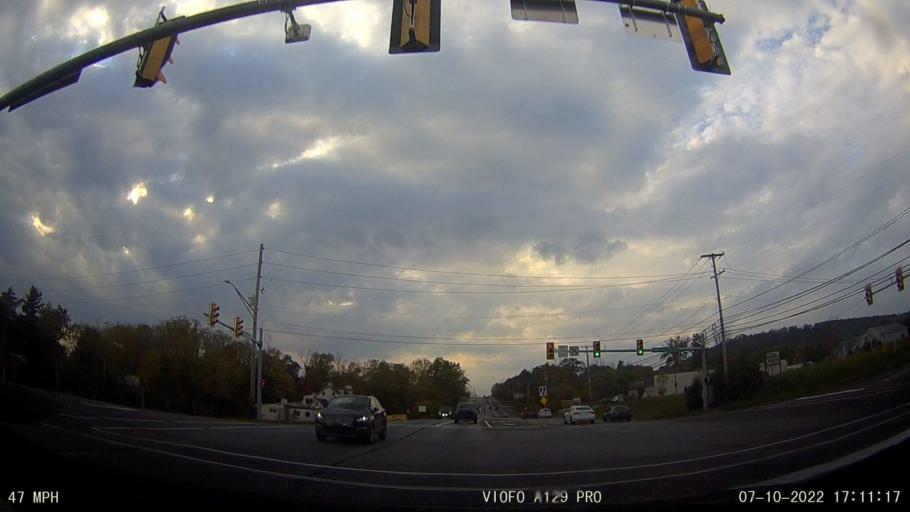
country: US
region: Pennsylvania
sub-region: Berks County
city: Amity Gardens
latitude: 40.2649
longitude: -75.7519
